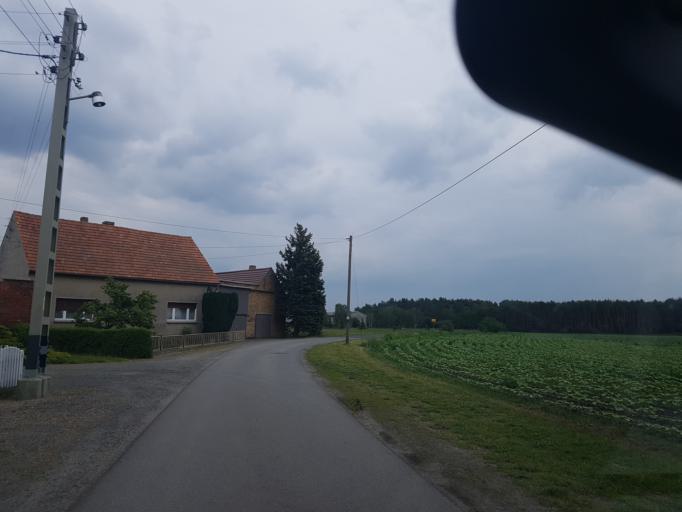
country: DE
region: Brandenburg
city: Finsterwalde
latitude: 51.5645
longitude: 13.6674
